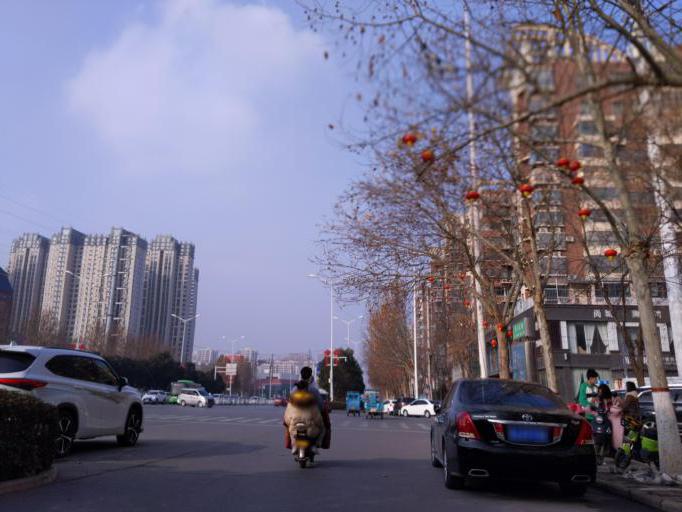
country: CN
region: Henan Sheng
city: Puyang
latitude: 35.7844
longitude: 115.0210
